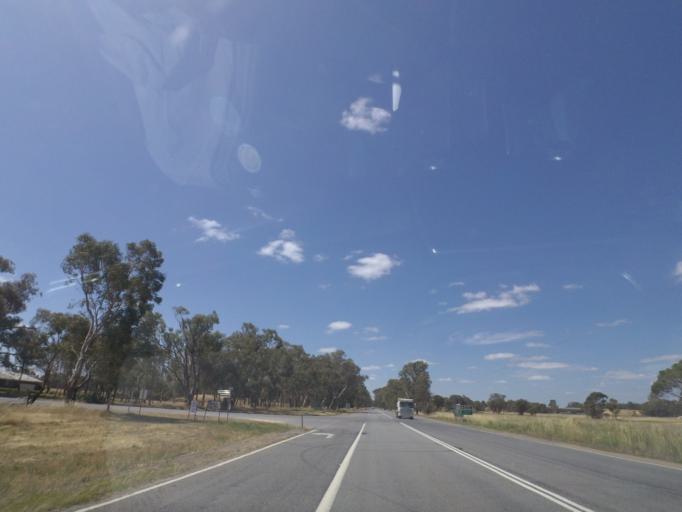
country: AU
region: Victoria
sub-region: Wangaratta
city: Wangaratta
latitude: -36.4124
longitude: 146.2678
